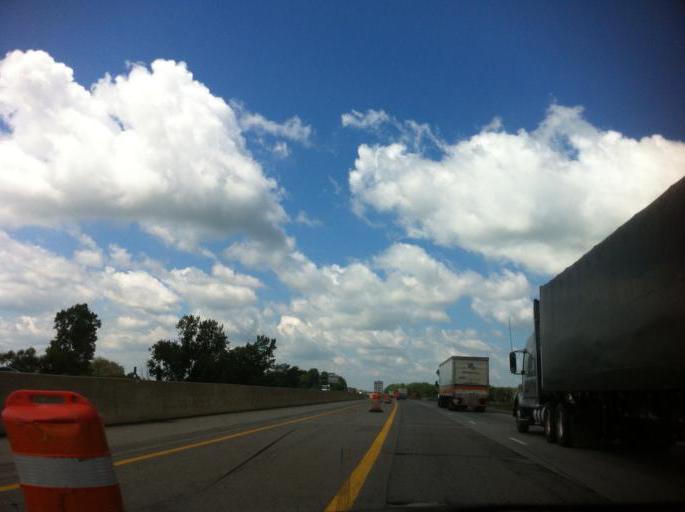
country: US
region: Ohio
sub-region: Huron County
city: Bellevue
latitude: 41.3471
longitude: -82.7995
